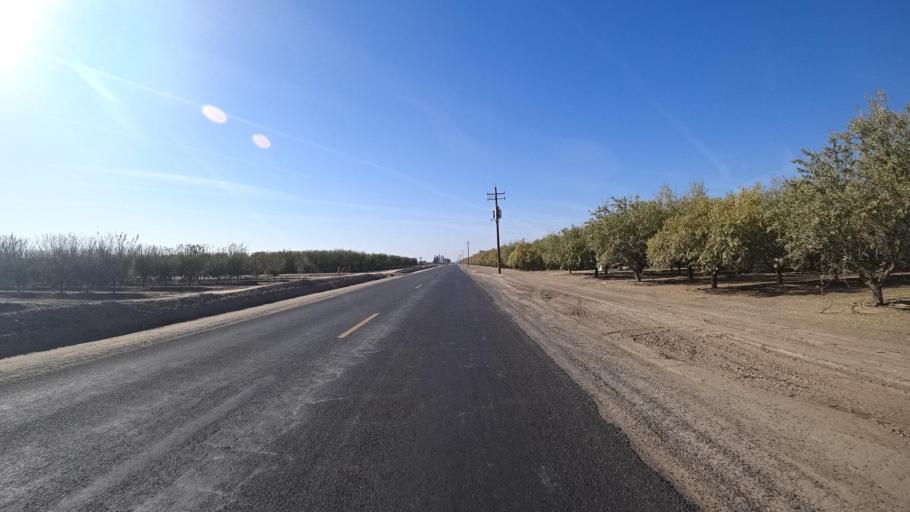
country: US
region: California
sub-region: Kern County
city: Wasco
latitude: 35.6452
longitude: -119.3160
